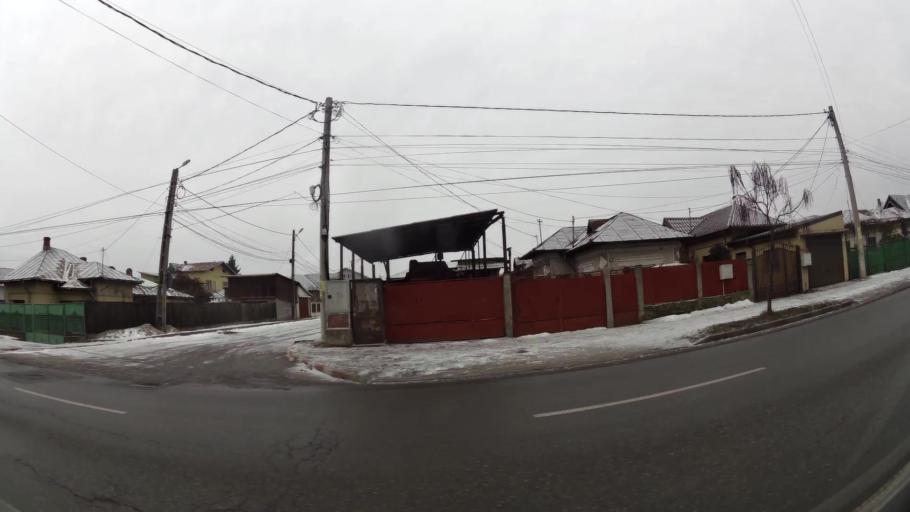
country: RO
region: Dambovita
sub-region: Comuna Ulmi
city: Ulmi
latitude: 44.9134
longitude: 25.4839
